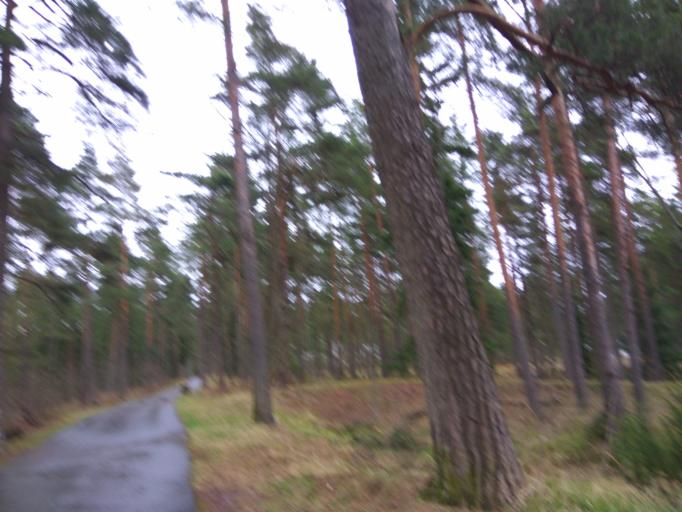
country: FI
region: Uusimaa
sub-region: Helsinki
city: Helsinki
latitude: 60.2213
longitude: 24.9539
